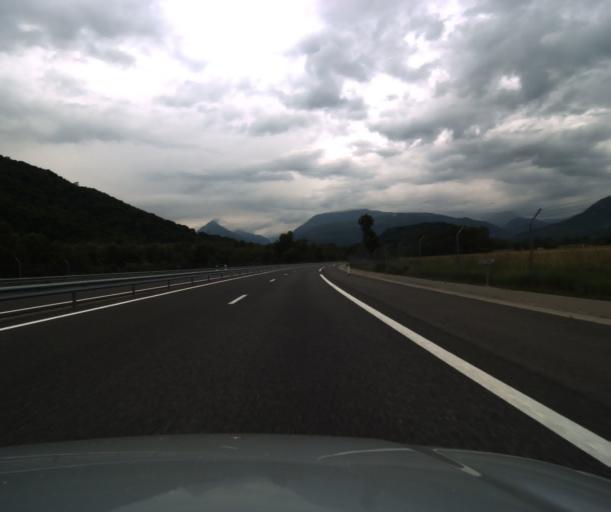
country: FR
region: Midi-Pyrenees
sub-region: Departement des Hautes-Pyrenees
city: Argeles-Gazost
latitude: 43.0334
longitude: -0.0642
